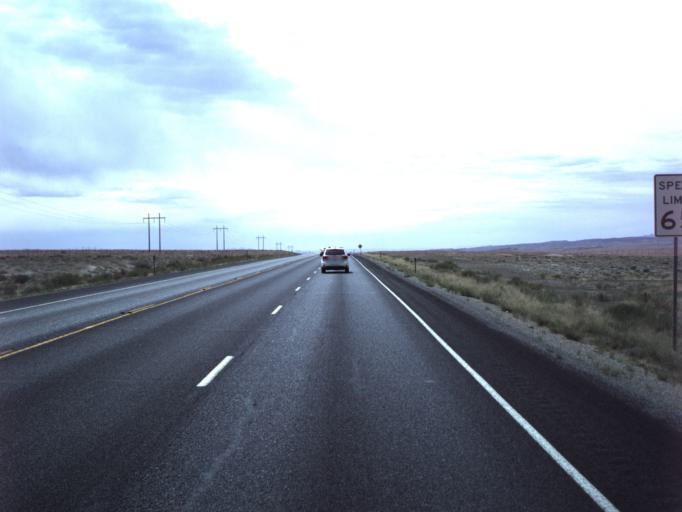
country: US
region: Utah
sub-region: Carbon County
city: East Carbon City
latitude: 39.1881
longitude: -110.3385
